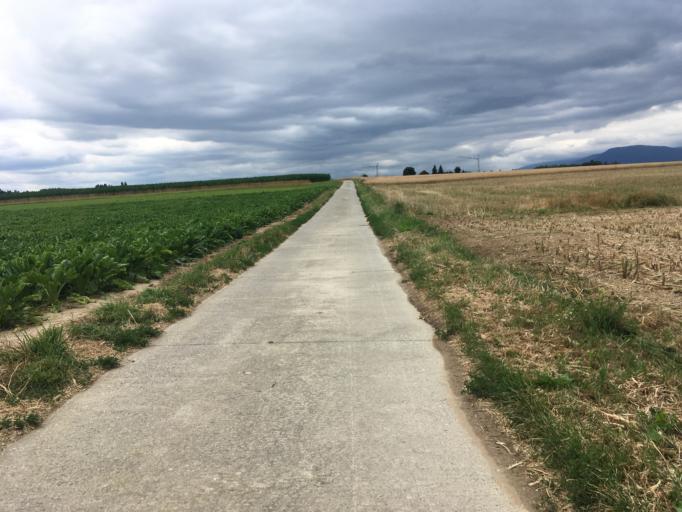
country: CH
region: Vaud
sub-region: Broye-Vully District
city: Payerne
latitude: 46.8748
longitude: 6.9129
